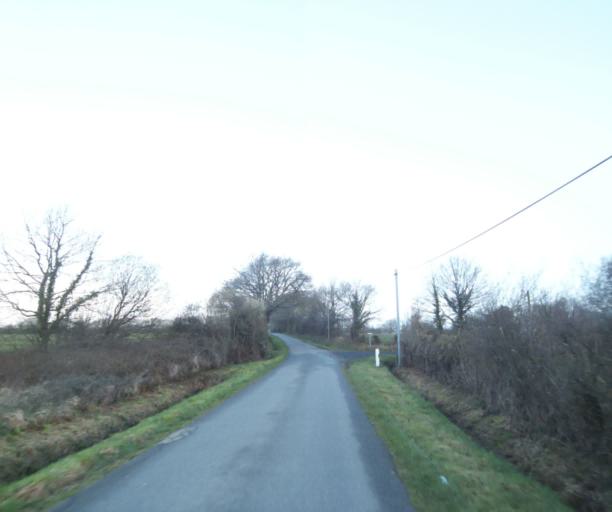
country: FR
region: Pays de la Loire
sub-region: Departement de la Loire-Atlantique
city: Malville
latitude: 47.3857
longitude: -1.8985
